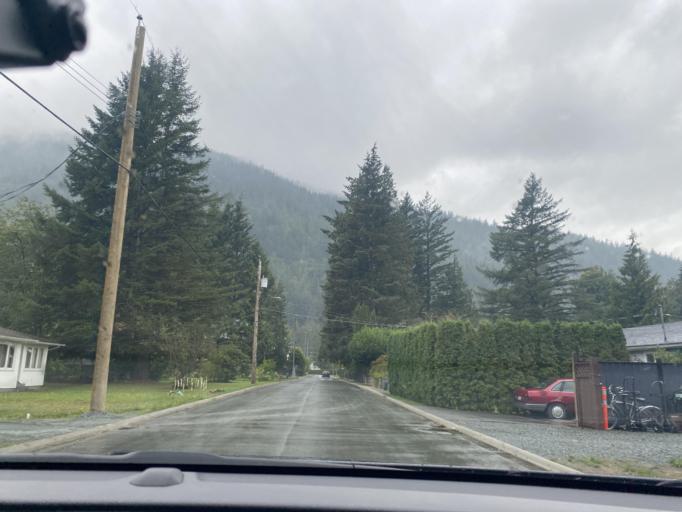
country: CA
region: British Columbia
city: Agassiz
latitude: 49.2942
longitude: -121.7788
